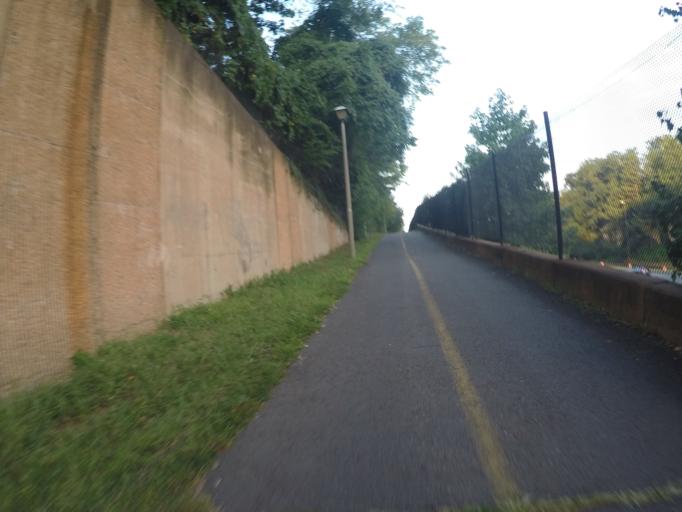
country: US
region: Virginia
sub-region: Arlington County
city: Arlington
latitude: 38.8886
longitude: -77.1136
